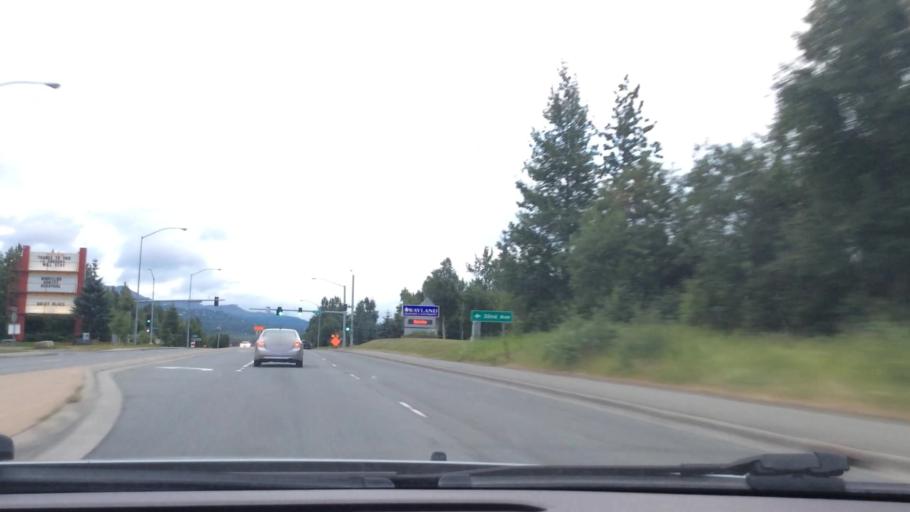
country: US
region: Alaska
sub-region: Anchorage Municipality
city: Elmendorf Air Force Base
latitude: 61.1932
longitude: -149.7335
